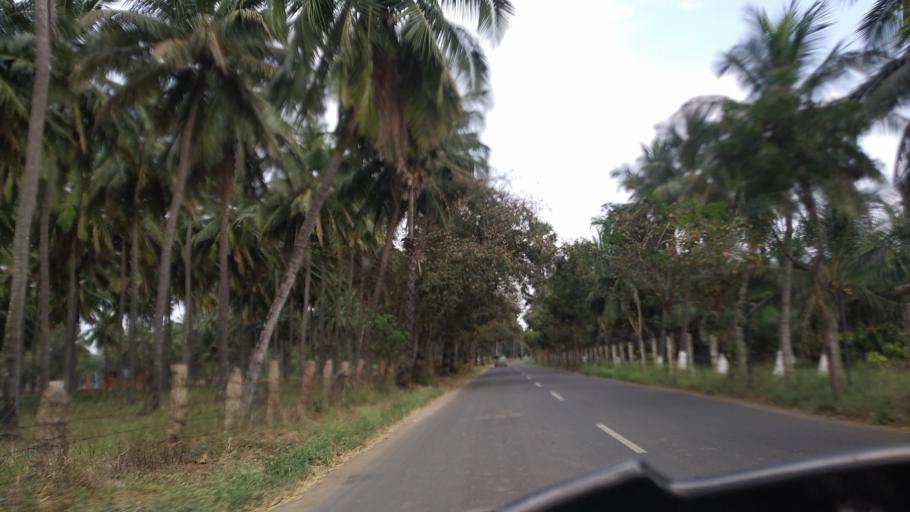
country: IN
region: Tamil Nadu
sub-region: Coimbatore
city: Perur
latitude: 10.9589
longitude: 76.7502
